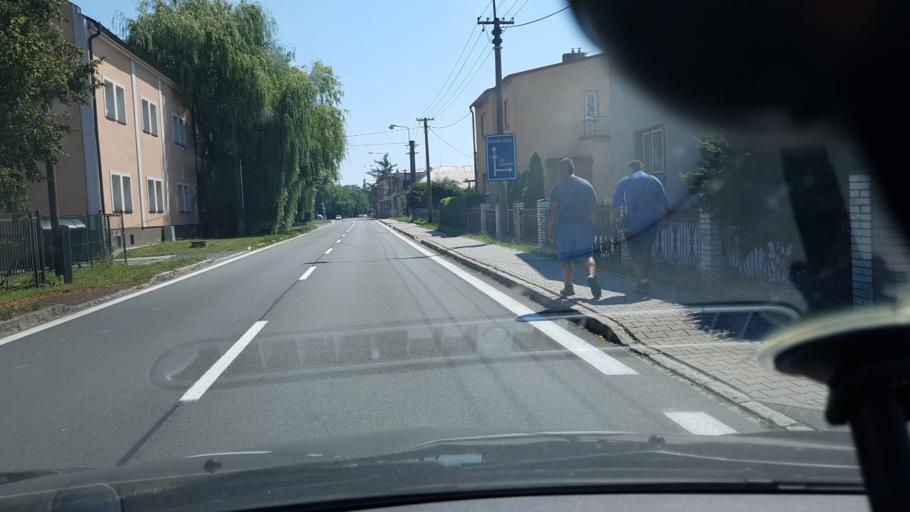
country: CZ
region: Moravskoslezsky
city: Bohumin
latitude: 49.9064
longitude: 18.3453
